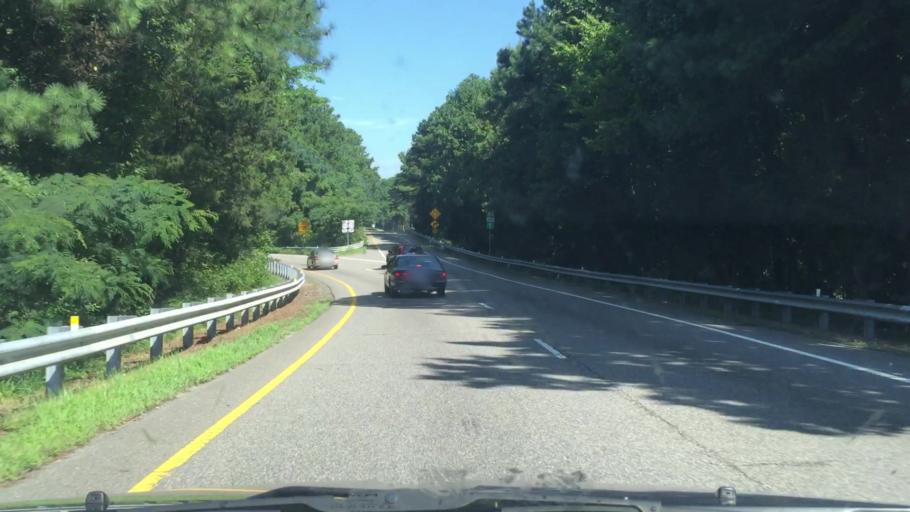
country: US
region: Virginia
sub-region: Henrico County
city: Dumbarton
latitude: 37.5982
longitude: -77.4896
